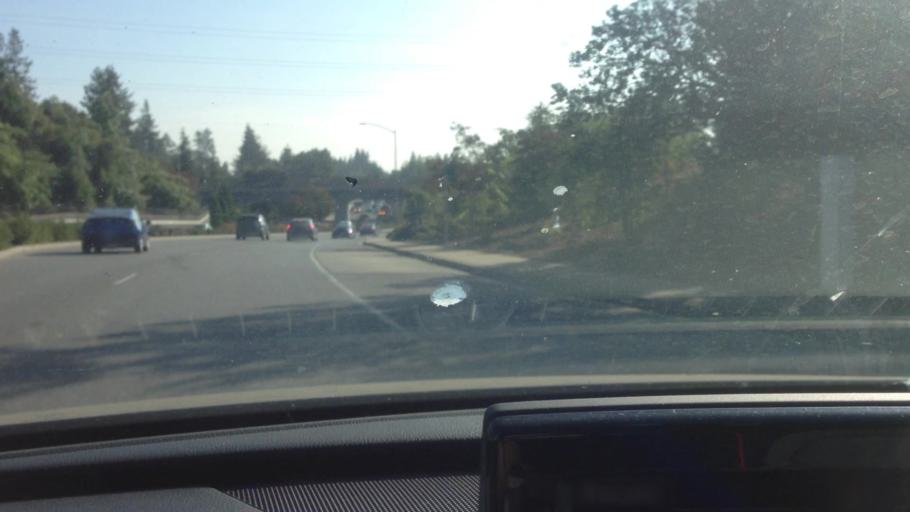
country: US
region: California
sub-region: Santa Clara County
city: Saratoga
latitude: 37.2753
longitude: -122.0096
